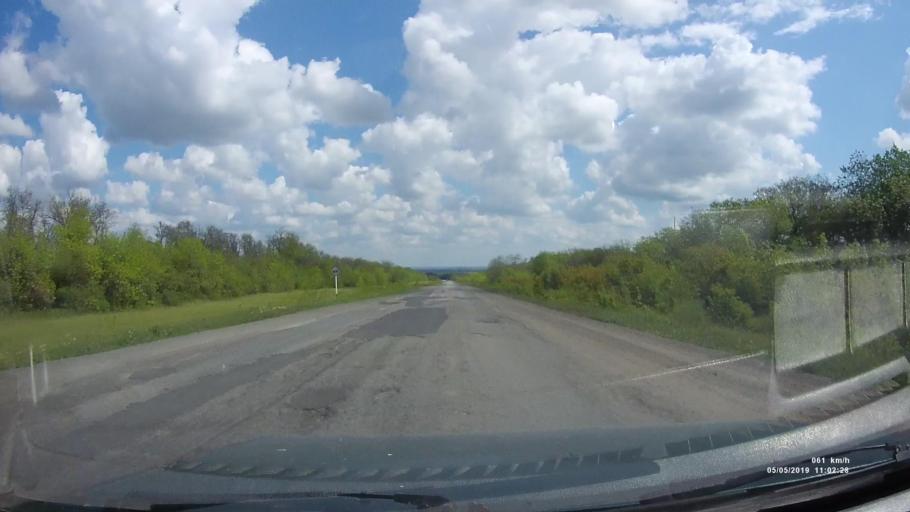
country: RU
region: Rostov
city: Ust'-Donetskiy
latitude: 47.6849
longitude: 40.9087
